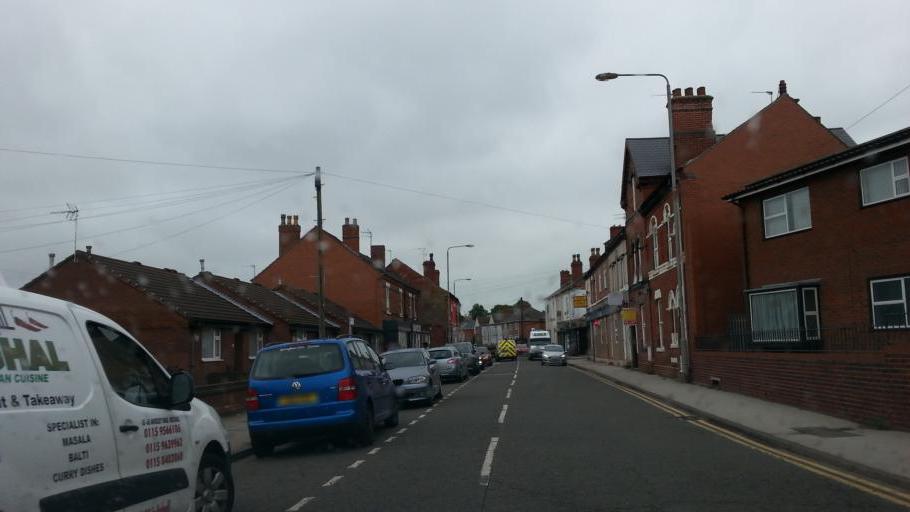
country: GB
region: England
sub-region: Nottinghamshire
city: Hucknall
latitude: 53.0352
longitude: -1.2050
